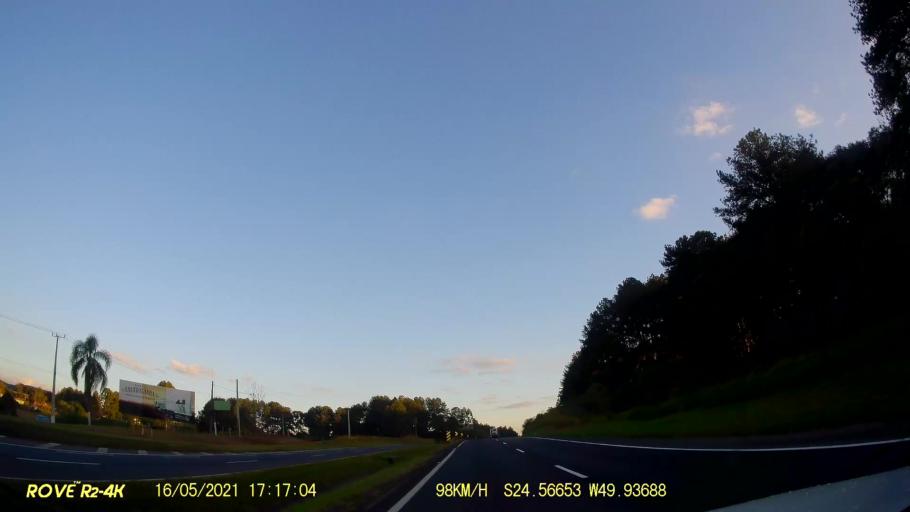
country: BR
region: Parana
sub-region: Pirai Do Sul
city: Pirai do Sul
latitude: -24.5668
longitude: -49.9369
